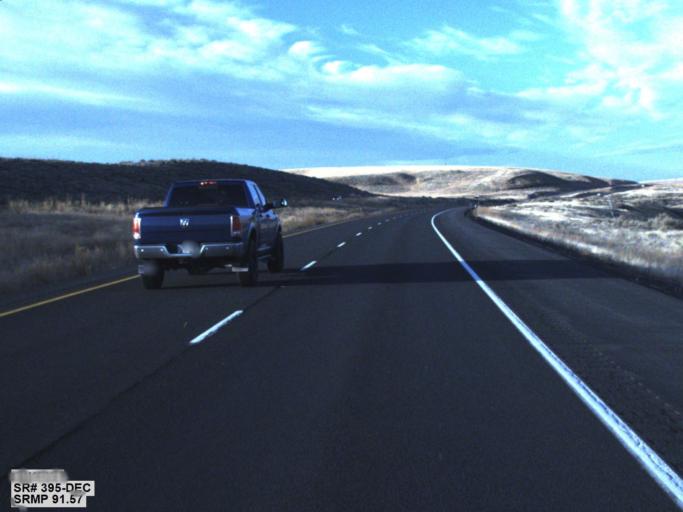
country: US
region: Washington
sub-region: Adams County
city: Ritzville
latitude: 47.0552
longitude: -118.4197
